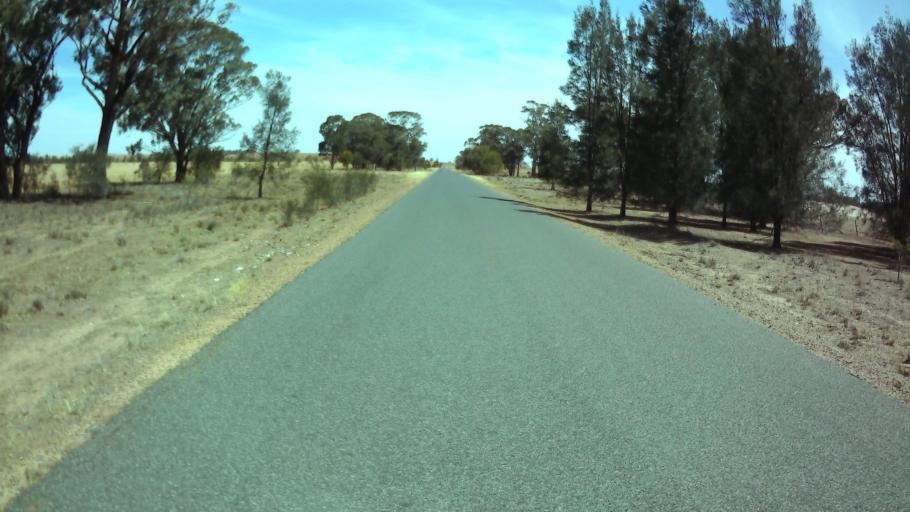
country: AU
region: New South Wales
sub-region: Weddin
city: Grenfell
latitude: -33.8816
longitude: 147.7428
